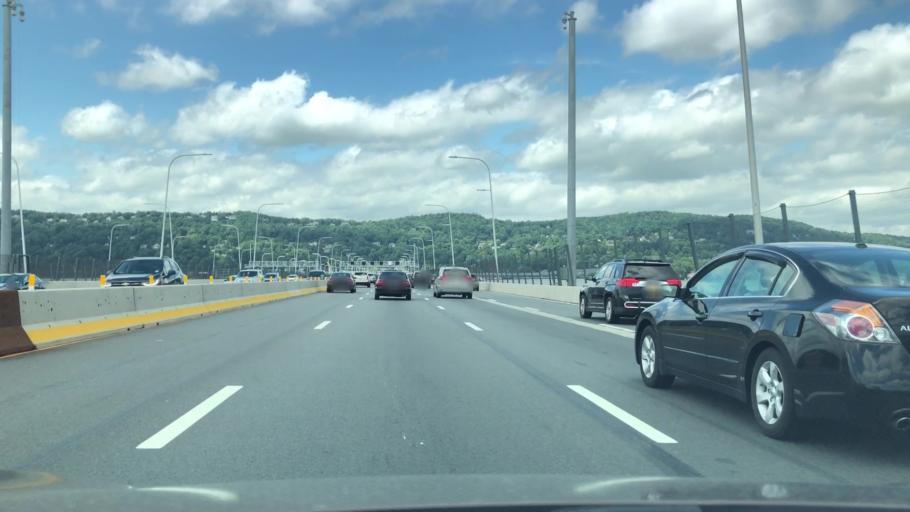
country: US
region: New York
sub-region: Rockland County
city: South Nyack
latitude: 41.0715
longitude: -73.8958
